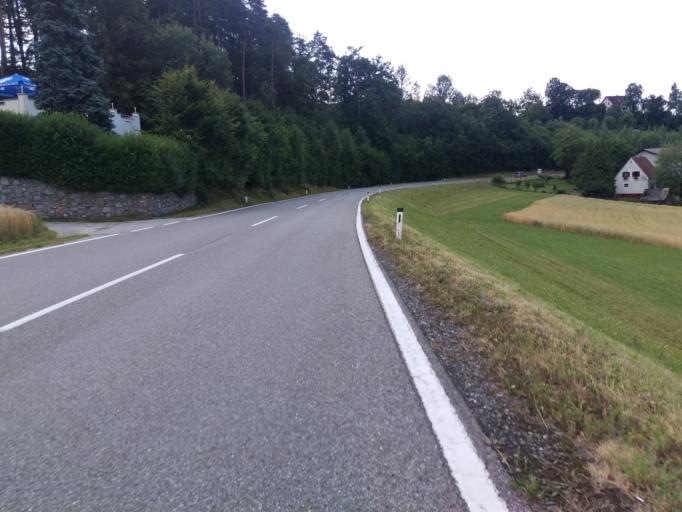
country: AT
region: Styria
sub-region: Politischer Bezirk Graz-Umgebung
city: Kumberg
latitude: 47.1354
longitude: 15.5171
